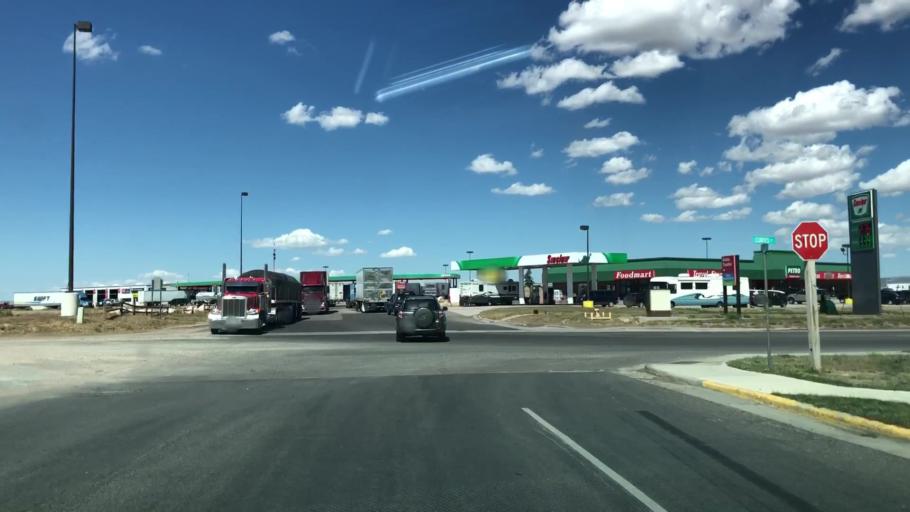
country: US
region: Wyoming
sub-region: Albany County
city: Laramie
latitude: 41.3275
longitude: -105.6202
